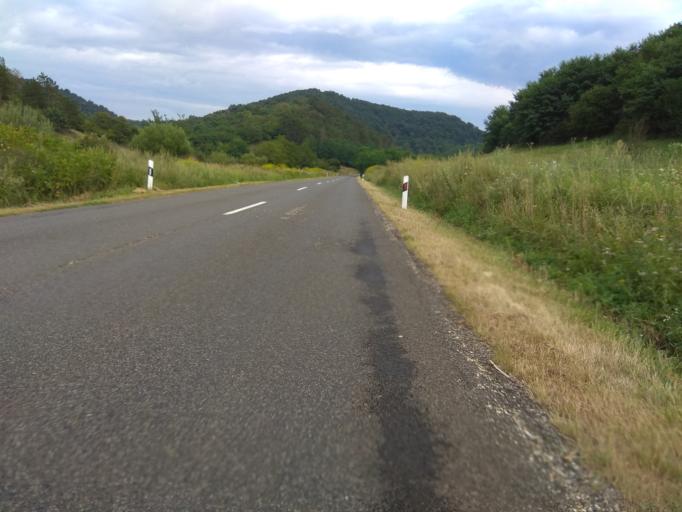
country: HU
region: Heves
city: Tarnalelesz
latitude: 48.0600
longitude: 20.2040
